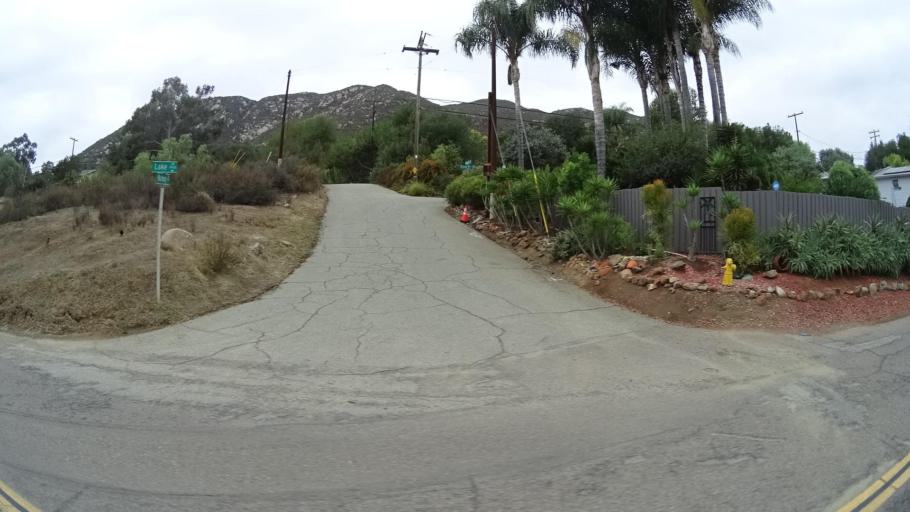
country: US
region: California
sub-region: San Diego County
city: Escondido
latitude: 33.0729
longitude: -117.1181
